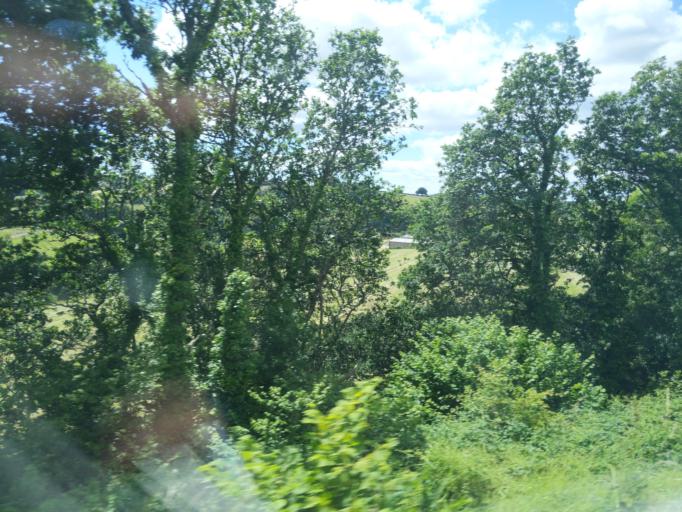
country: GB
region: England
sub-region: Cornwall
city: Liskeard
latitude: 50.4231
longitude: -4.3936
